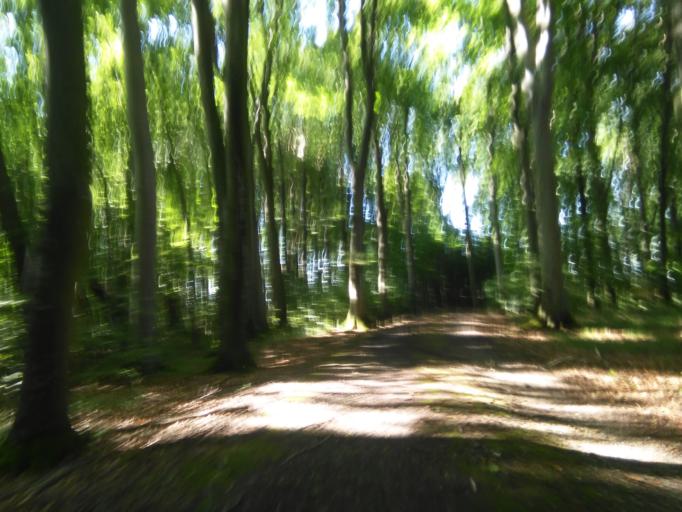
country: DK
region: Central Jutland
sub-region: Odder Kommune
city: Odder
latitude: 55.9538
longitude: 10.0787
